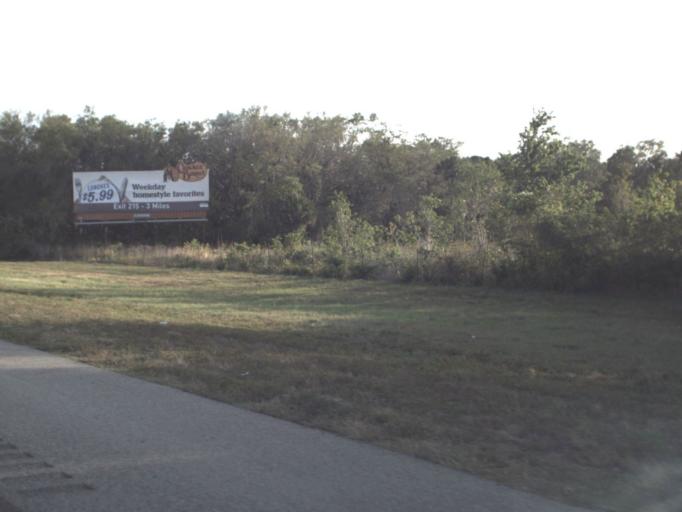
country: US
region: Florida
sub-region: Brevard County
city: Titusville
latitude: 28.5968
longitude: -80.8515
